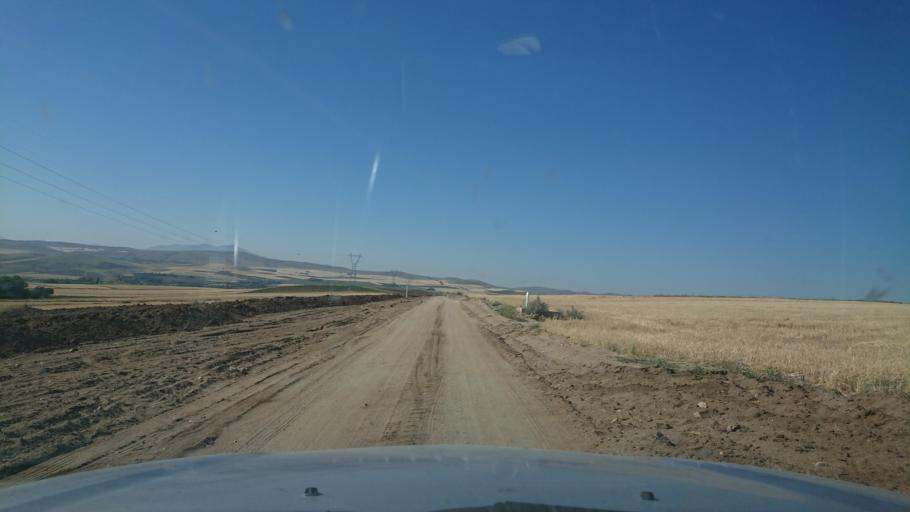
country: TR
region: Aksaray
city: Agacoren
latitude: 38.8412
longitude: 33.9442
